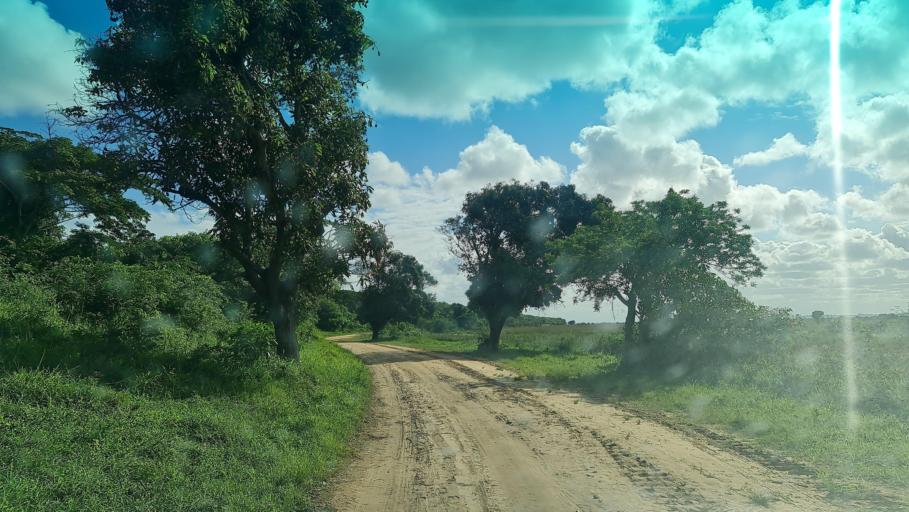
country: MZ
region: Maputo
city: Manhica
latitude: -25.4292
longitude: 32.8942
